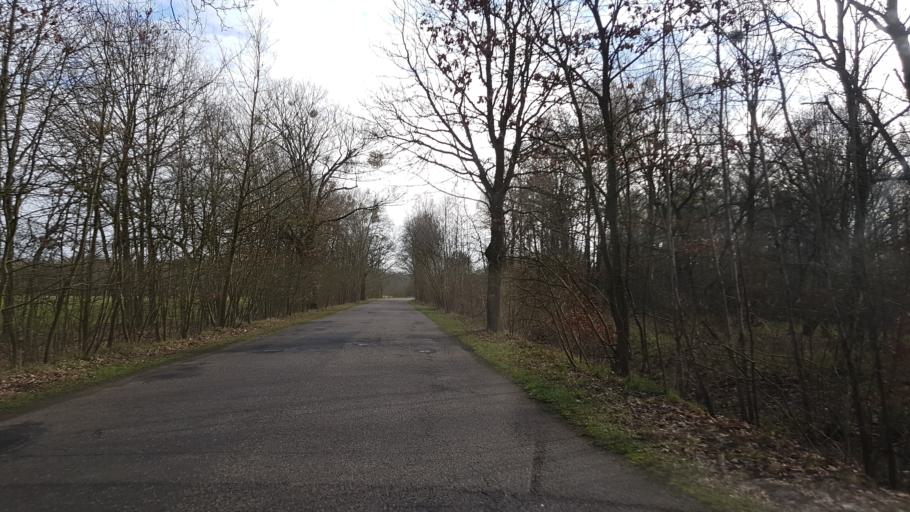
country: PL
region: West Pomeranian Voivodeship
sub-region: Powiat policki
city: Dobra
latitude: 53.5333
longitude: 14.3226
